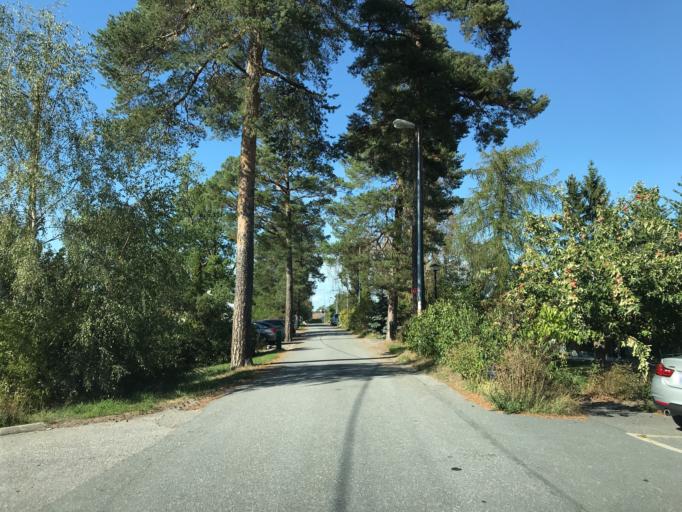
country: SE
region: Stockholm
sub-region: Sollentuna Kommun
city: Sollentuna
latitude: 59.4236
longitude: 17.9670
